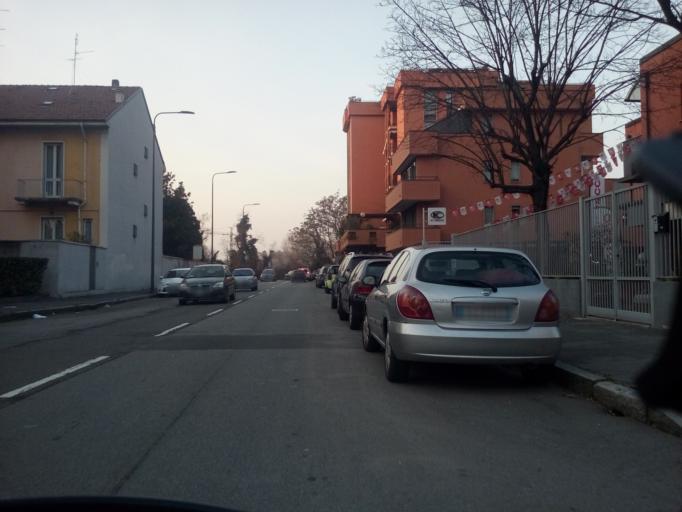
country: IT
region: Lombardy
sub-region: Citta metropolitana di Milano
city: Cesano Boscone
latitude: 45.4605
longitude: 9.0837
